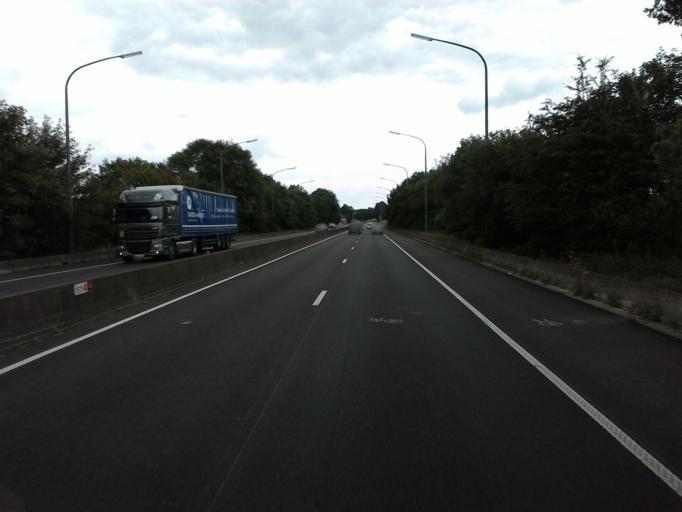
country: BE
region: Wallonia
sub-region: Province du Luxembourg
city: Martelange
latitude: 49.8718
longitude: 5.7100
